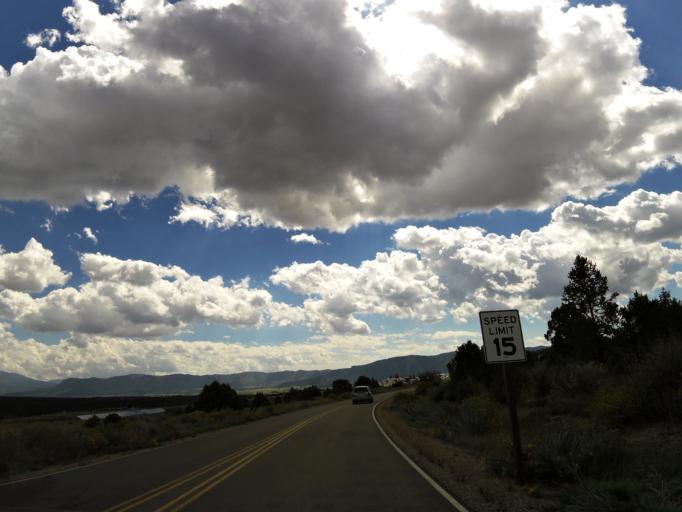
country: US
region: Colorado
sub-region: Montezuma County
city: Mancos
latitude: 37.3387
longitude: -108.4109
